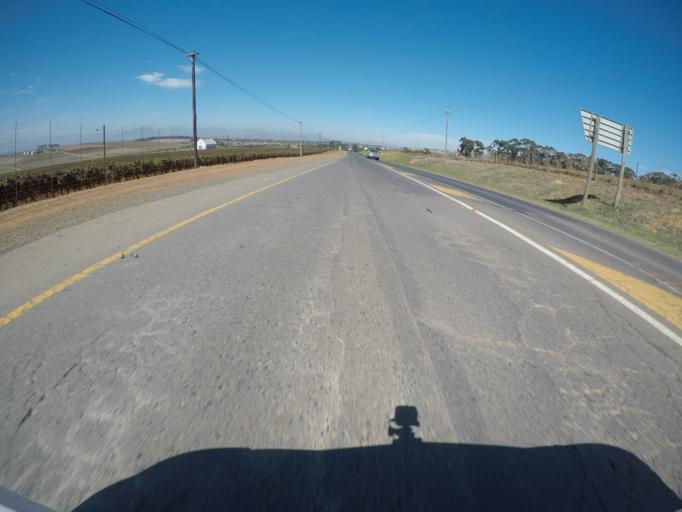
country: ZA
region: Western Cape
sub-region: City of Cape Town
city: Kraaifontein
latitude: -33.8036
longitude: 18.6203
